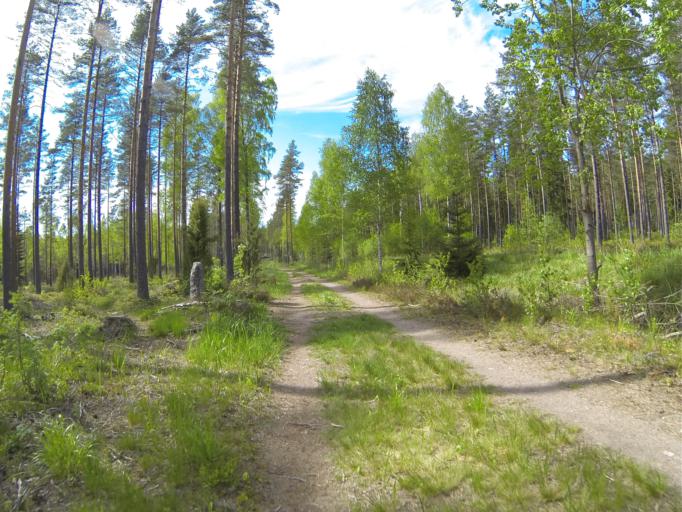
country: FI
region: Varsinais-Suomi
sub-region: Salo
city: Salo
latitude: 60.3878
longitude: 23.2043
